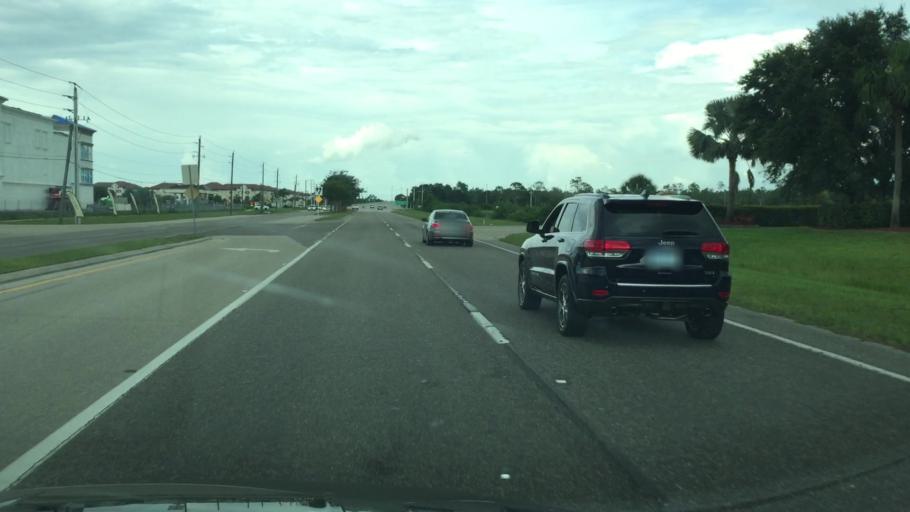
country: US
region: Florida
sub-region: Lee County
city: Estero
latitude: 26.4493
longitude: -81.7935
